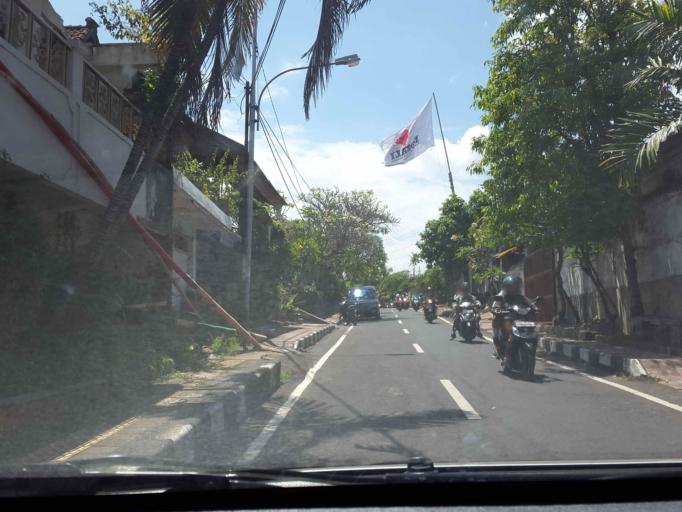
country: ID
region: Bali
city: Semarapura
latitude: -8.5350
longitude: 115.4013
